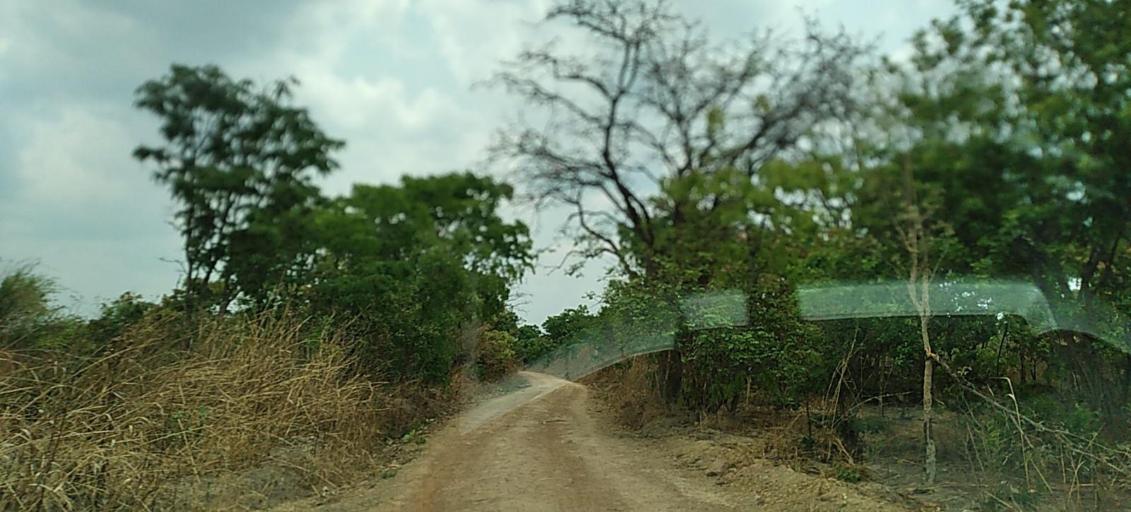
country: ZM
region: Copperbelt
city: Chililabombwe
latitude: -12.3165
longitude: 27.7904
